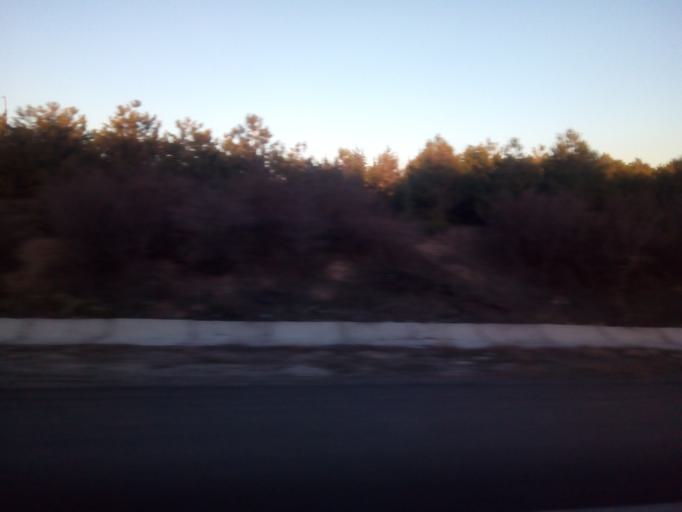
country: TR
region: Ankara
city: Etimesgut
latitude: 40.0194
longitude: 32.6240
